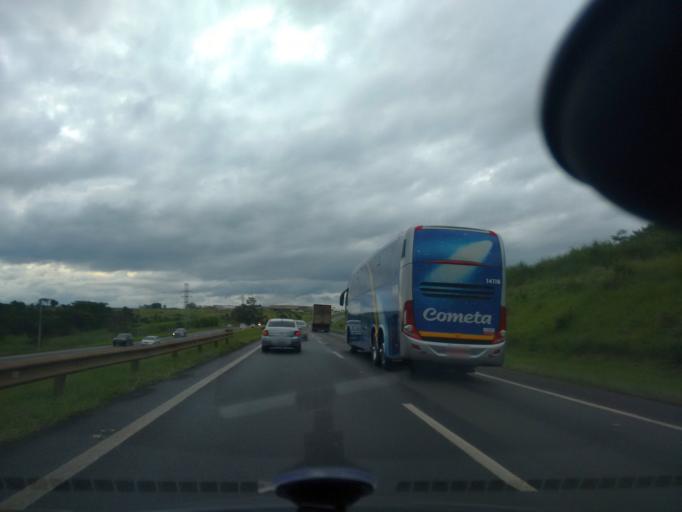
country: BR
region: Sao Paulo
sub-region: Santa Gertrudes
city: Santa Gertrudes
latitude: -22.4531
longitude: -47.5542
